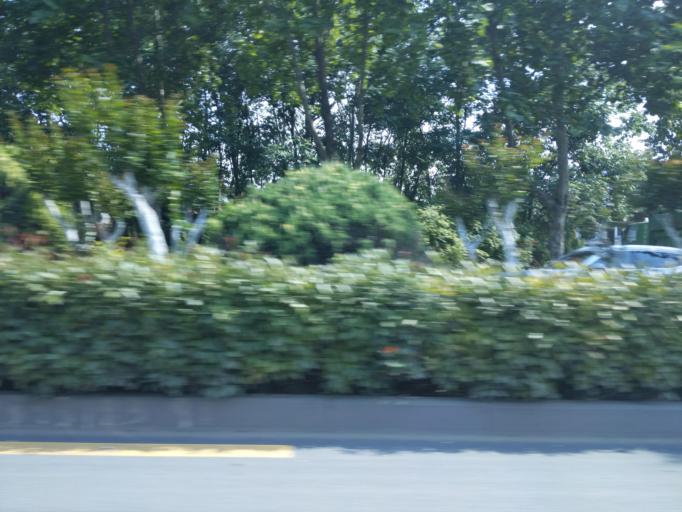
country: CN
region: Henan Sheng
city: Puyang
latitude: 35.7743
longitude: 114.9540
